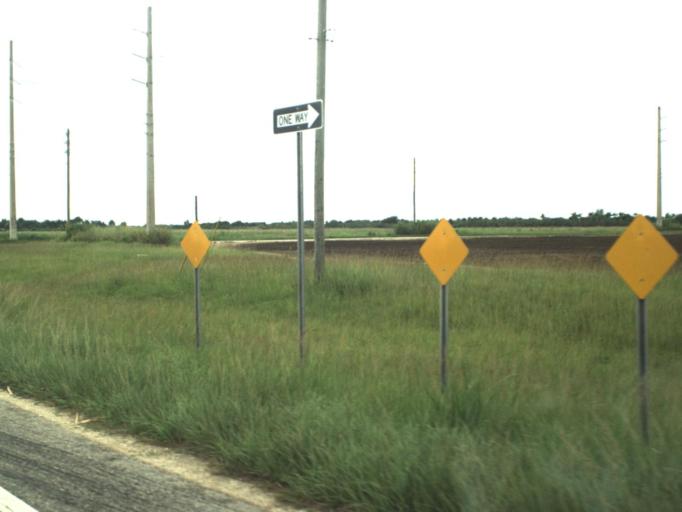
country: US
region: Florida
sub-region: Miami-Dade County
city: Country Walk
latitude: 25.6388
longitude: -80.4799
